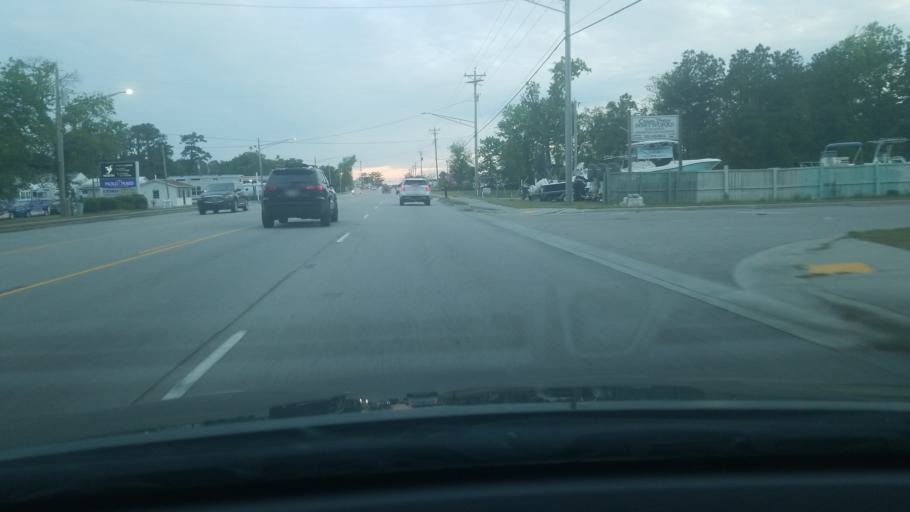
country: US
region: North Carolina
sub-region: Carteret County
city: Cedar Point
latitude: 34.6852
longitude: -77.0787
